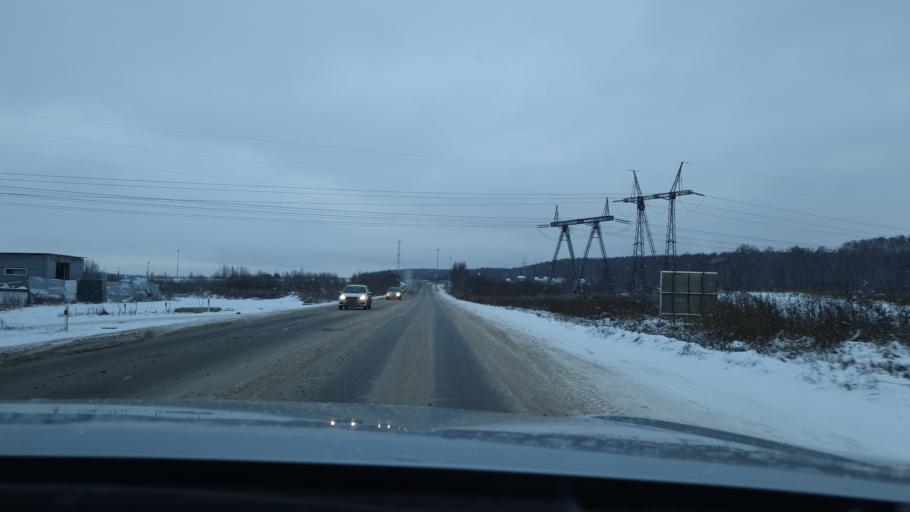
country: RU
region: Sverdlovsk
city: Istok
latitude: 56.7740
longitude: 60.7383
